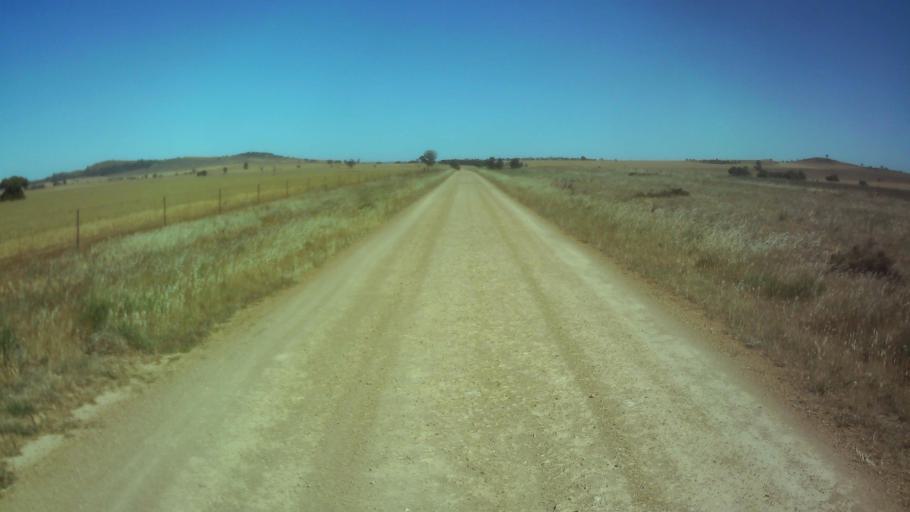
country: AU
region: New South Wales
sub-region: Weddin
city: Grenfell
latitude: -33.9789
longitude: 148.3263
